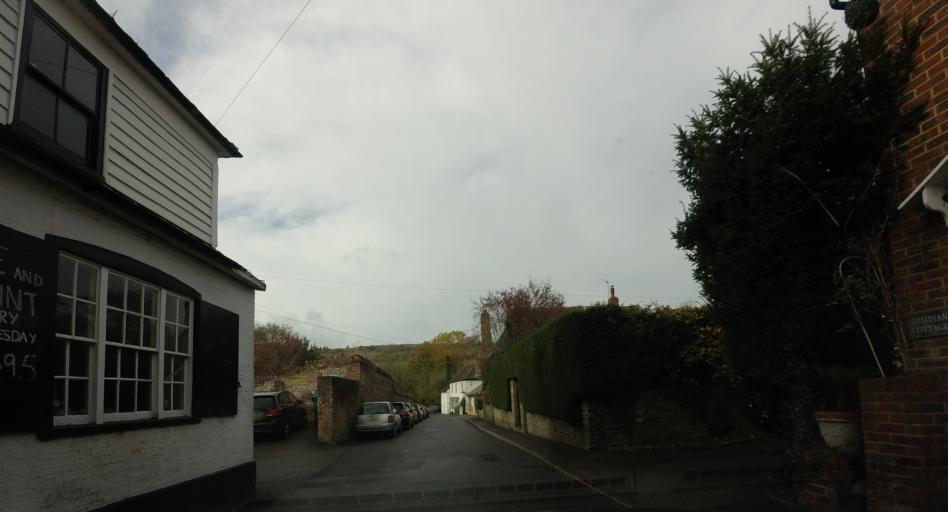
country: GB
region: England
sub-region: Kent
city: Shoreham
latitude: 51.3330
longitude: 0.1832
